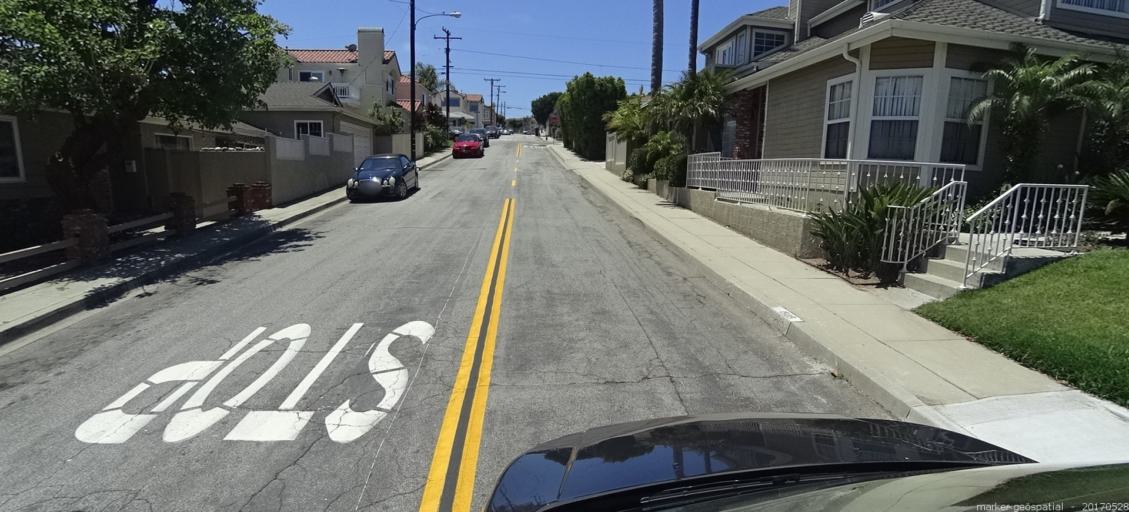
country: US
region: California
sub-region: Los Angeles County
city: Hermosa Beach
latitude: 33.8648
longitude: -118.3835
